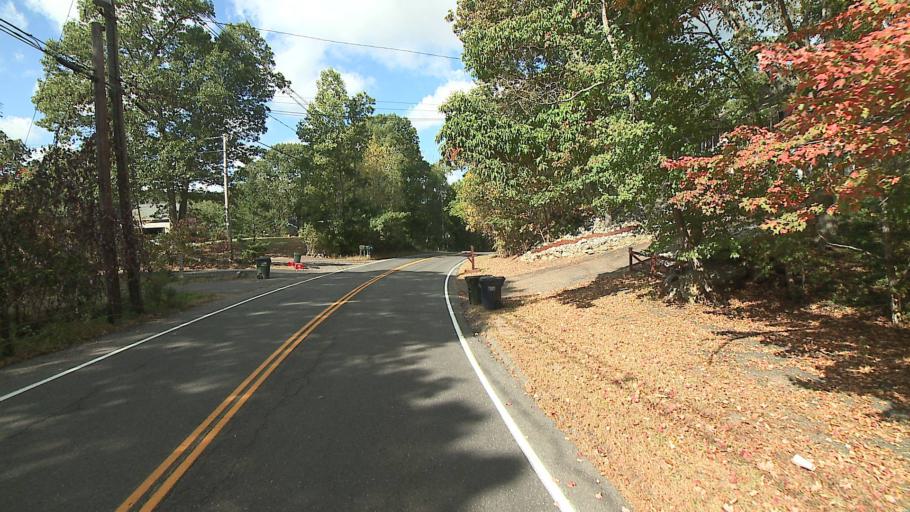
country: US
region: Connecticut
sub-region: New Haven County
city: Oxford
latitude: 41.4306
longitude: -73.1052
